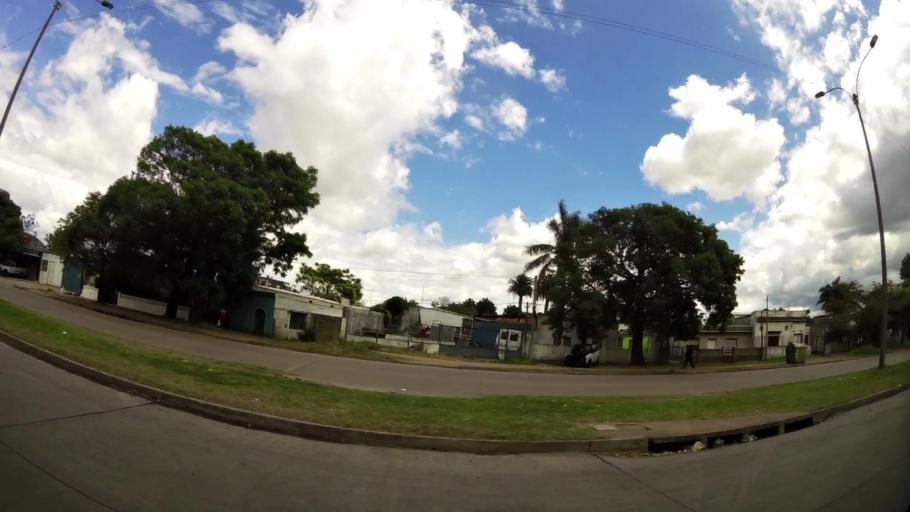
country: UY
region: Montevideo
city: Montevideo
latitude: -34.8340
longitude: -56.1451
